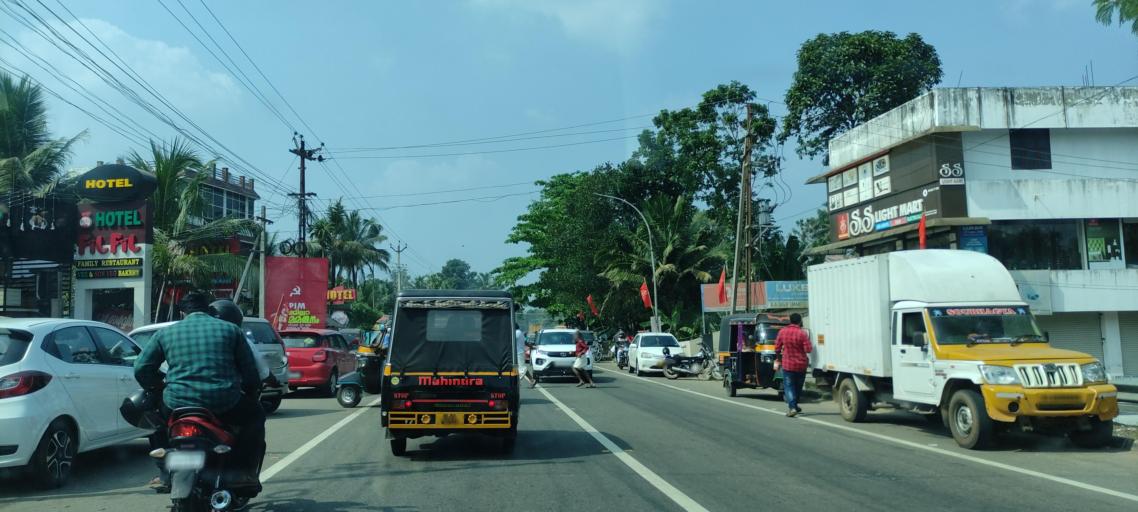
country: IN
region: Kerala
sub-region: Pattanamtitta
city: Adur
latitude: 9.1474
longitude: 76.7310
